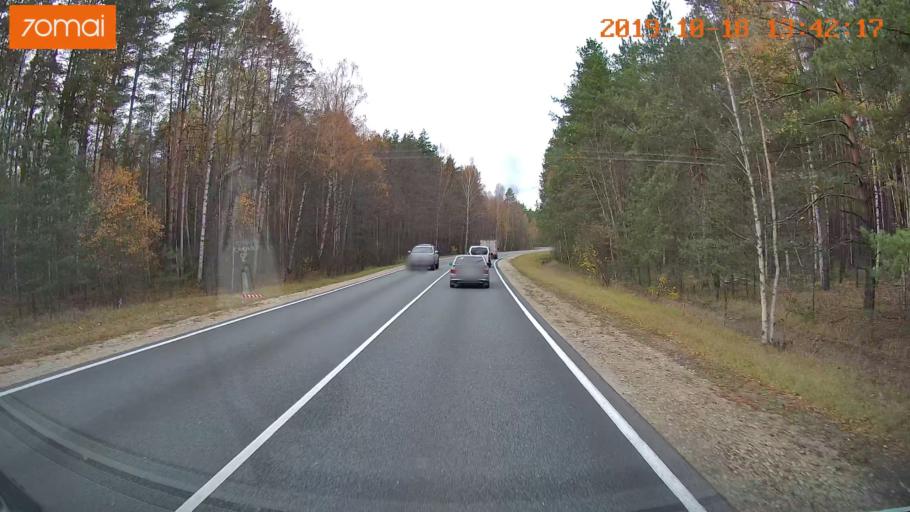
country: RU
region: Rjazan
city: Solotcha
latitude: 54.9252
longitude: 39.9914
